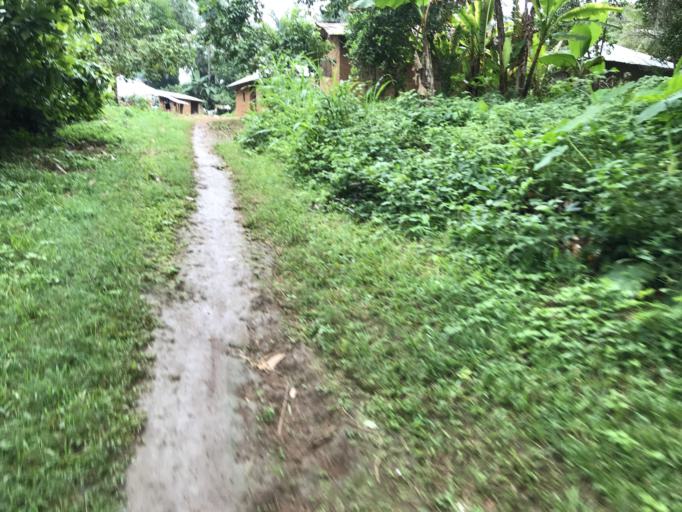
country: GN
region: Nzerekore
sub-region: Prefecture de Guekedou
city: Gueckedou
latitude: 8.4717
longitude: -10.3105
